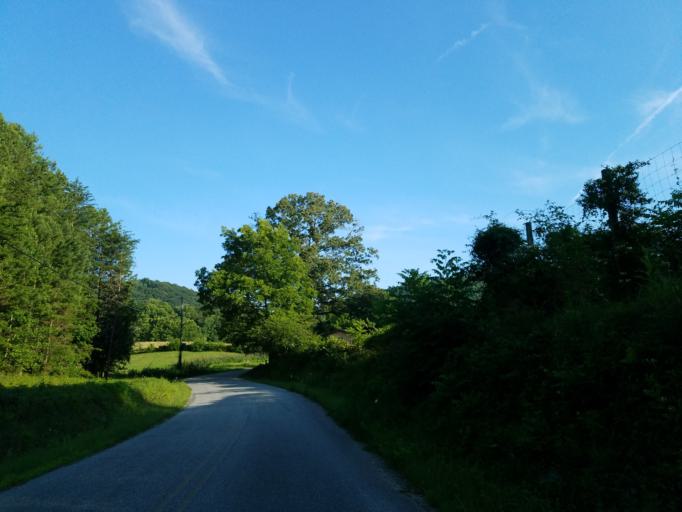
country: US
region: Georgia
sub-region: Gilmer County
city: Ellijay
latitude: 34.6327
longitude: -84.3317
